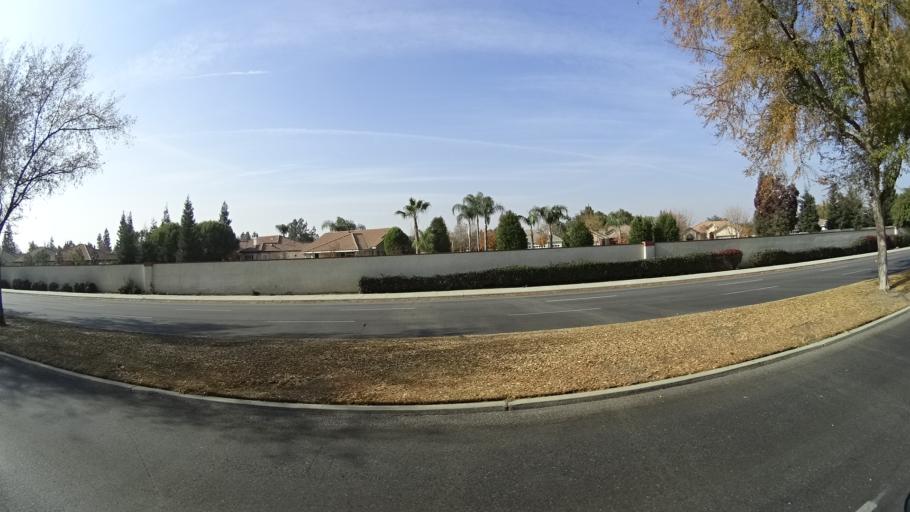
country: US
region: California
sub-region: Kern County
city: Greenacres
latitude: 35.3376
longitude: -119.1142
